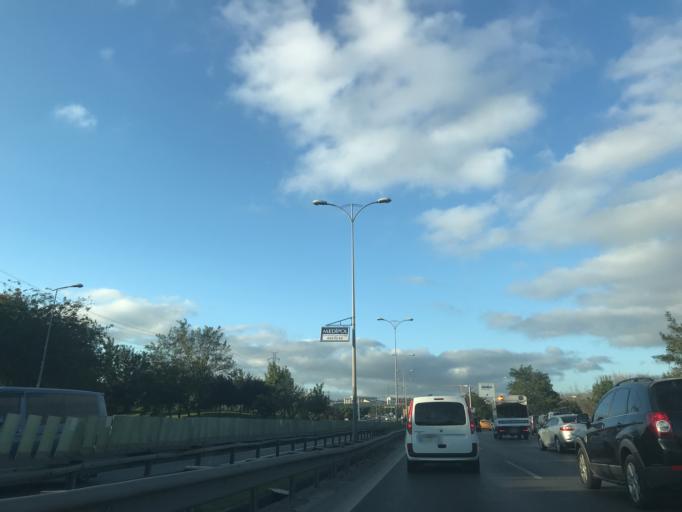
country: TR
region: Istanbul
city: Esenler
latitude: 41.0563
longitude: 28.8861
